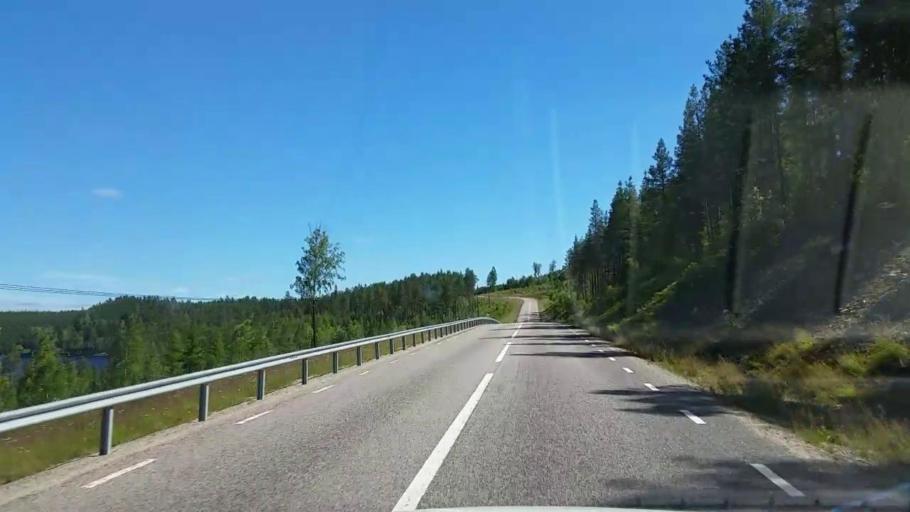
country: SE
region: Gaevleborg
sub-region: Ovanakers Kommun
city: Edsbyn
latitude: 61.5843
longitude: 15.6456
